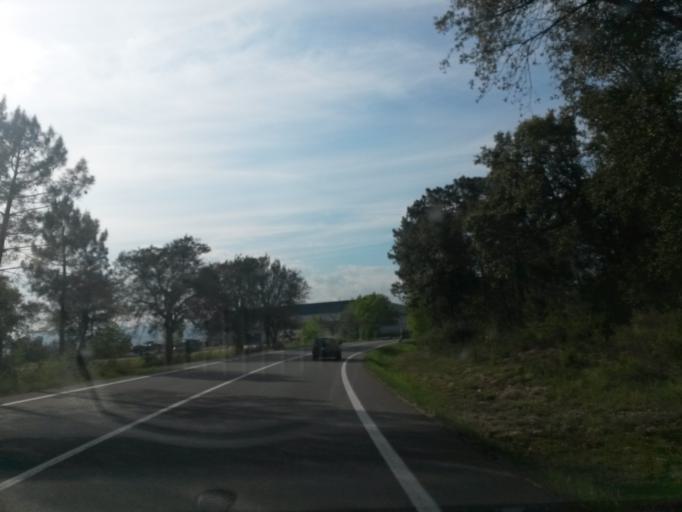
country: ES
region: Catalonia
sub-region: Provincia de Girona
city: Vilobi d'Onyar
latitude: 41.8482
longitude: 2.7751
